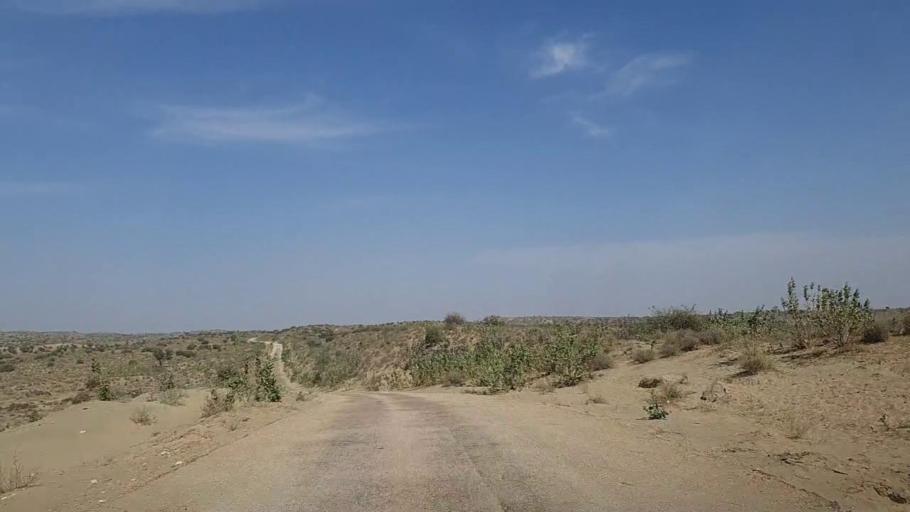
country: PK
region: Sindh
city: Umarkot
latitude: 25.2498
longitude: 69.9046
